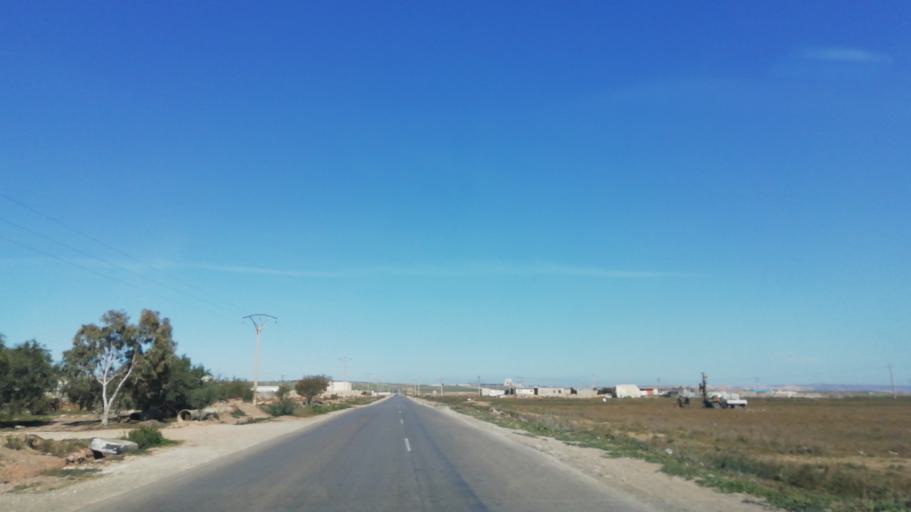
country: DZ
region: Oran
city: Es Senia
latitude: 35.5178
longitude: -0.5888
